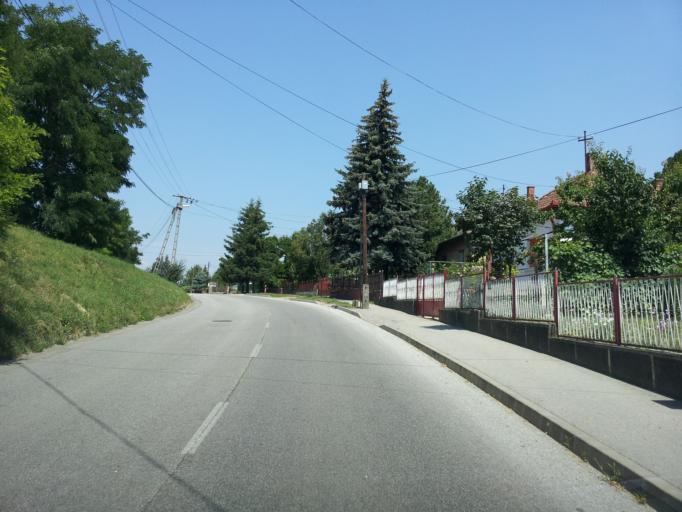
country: HU
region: Zala
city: Zalaegerszeg
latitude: 46.8556
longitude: 16.8447
